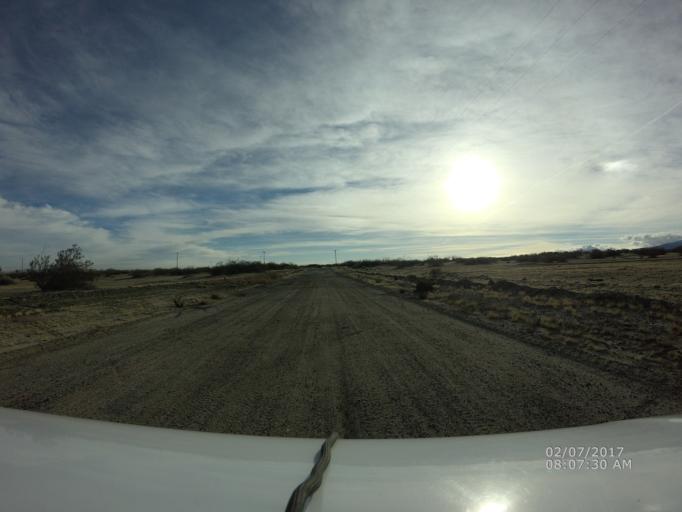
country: US
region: California
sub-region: Los Angeles County
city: Lake Los Angeles
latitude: 34.5724
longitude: -117.7219
